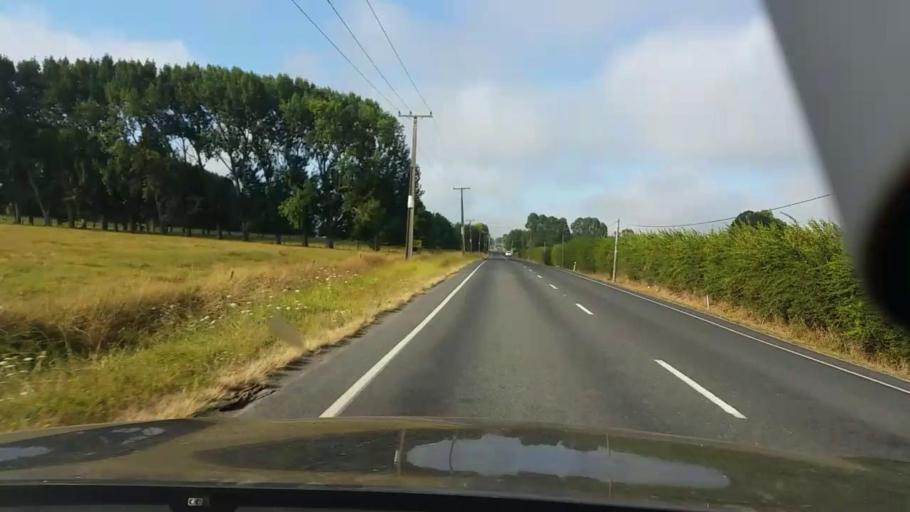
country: NZ
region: Waikato
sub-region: Hamilton City
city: Hamilton
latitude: -37.6011
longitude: 175.3523
